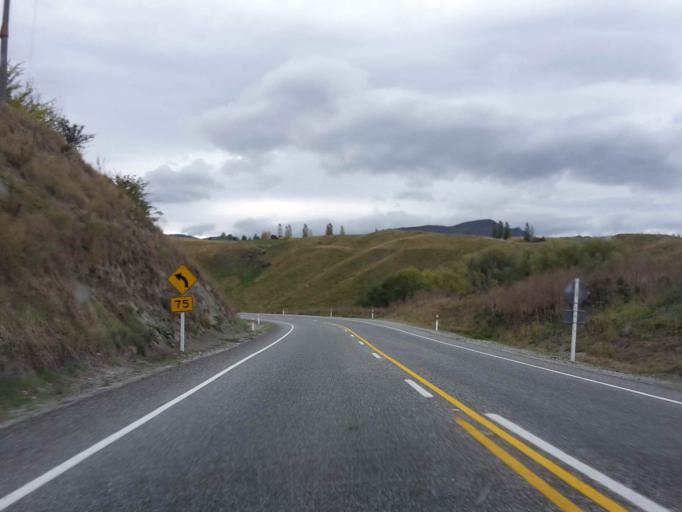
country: NZ
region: Otago
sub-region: Queenstown-Lakes District
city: Arrowtown
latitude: -44.9806
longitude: 168.8349
